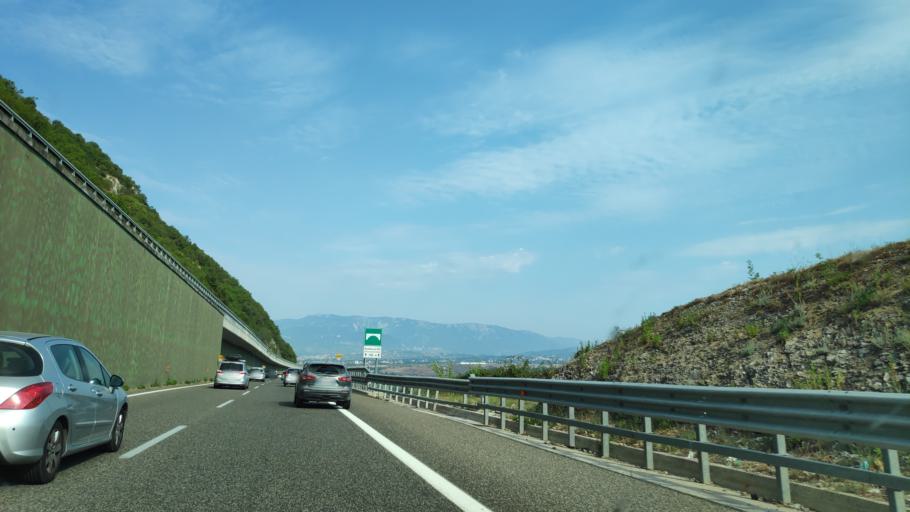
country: IT
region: Campania
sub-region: Provincia di Salerno
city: Sicignano degli Alburni
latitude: 40.5866
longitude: 15.3375
